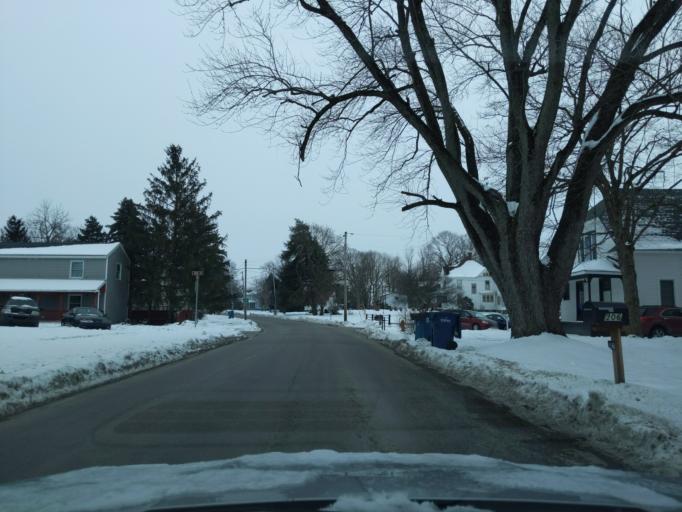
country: US
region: Indiana
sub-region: Benton County
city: Otterbein
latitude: 40.4873
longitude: -87.0962
